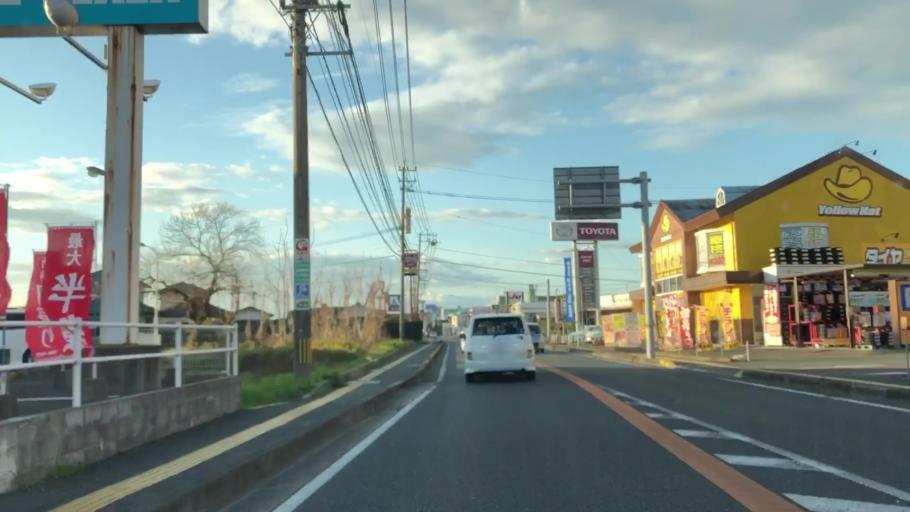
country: JP
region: Oita
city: Bungo-Takada-shi
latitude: 33.5293
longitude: 131.3378
